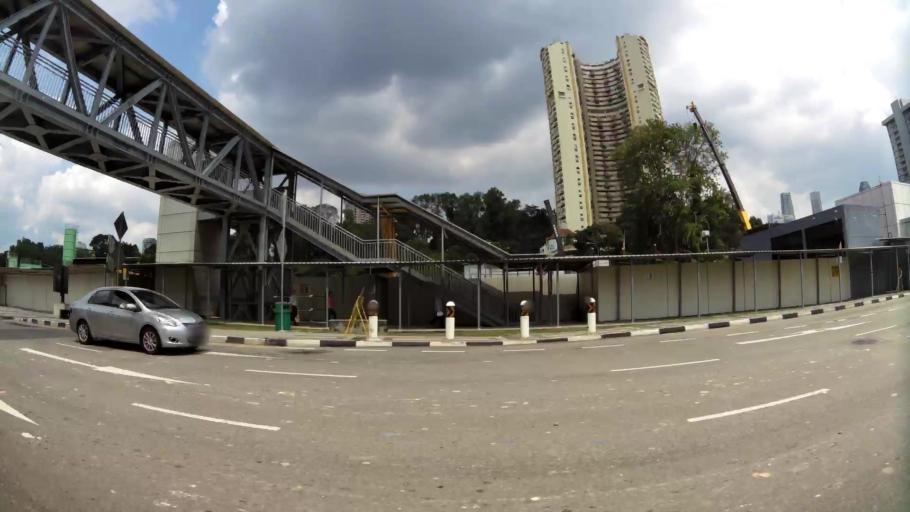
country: SG
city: Singapore
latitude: 1.2817
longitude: 103.8385
